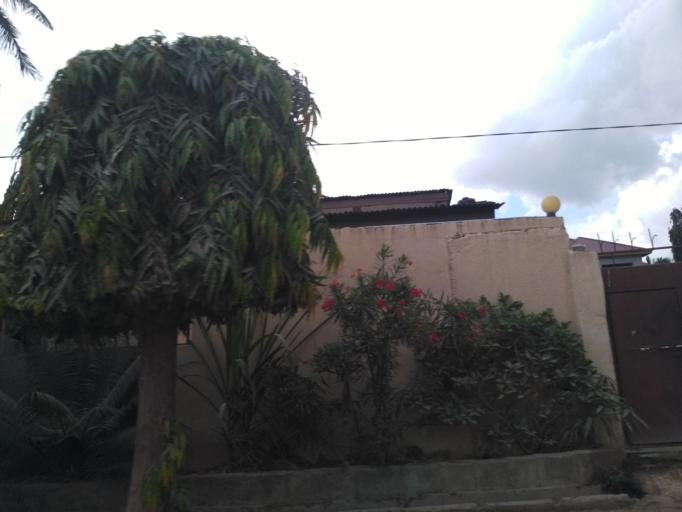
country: TZ
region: Dar es Salaam
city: Magomeni
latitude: -6.7553
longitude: 39.2406
